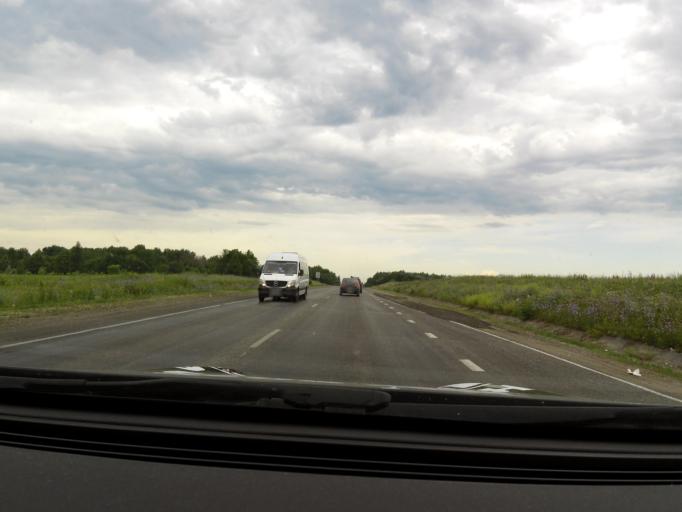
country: RU
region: Bashkortostan
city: Kudeyevskiy
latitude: 54.8171
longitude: 56.7877
